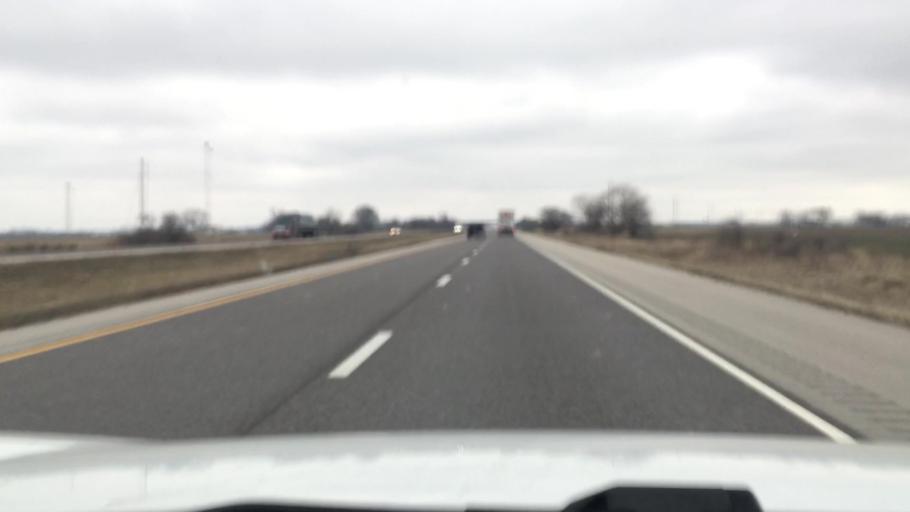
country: US
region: Illinois
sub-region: Fayette County
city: Saint Elmo
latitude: 39.0238
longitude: -88.8139
